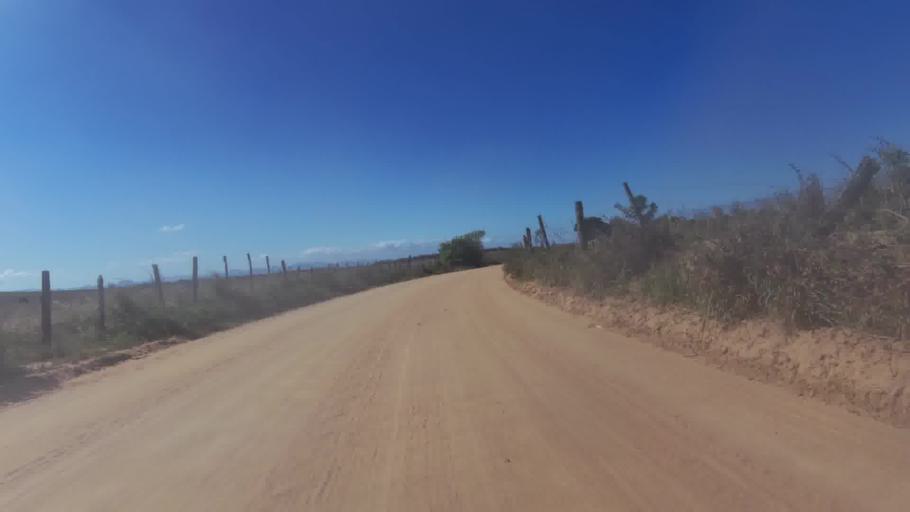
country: BR
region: Espirito Santo
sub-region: Marataizes
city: Marataizes
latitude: -21.1366
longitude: -40.9927
